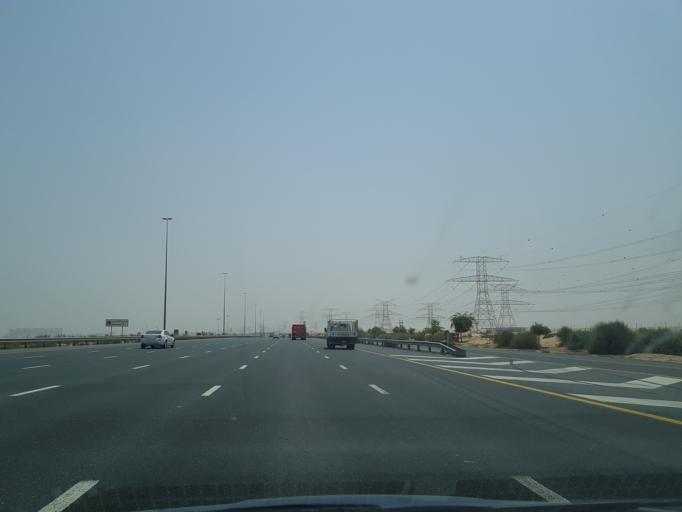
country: AE
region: Dubai
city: Dubai
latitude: 25.0658
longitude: 55.3446
